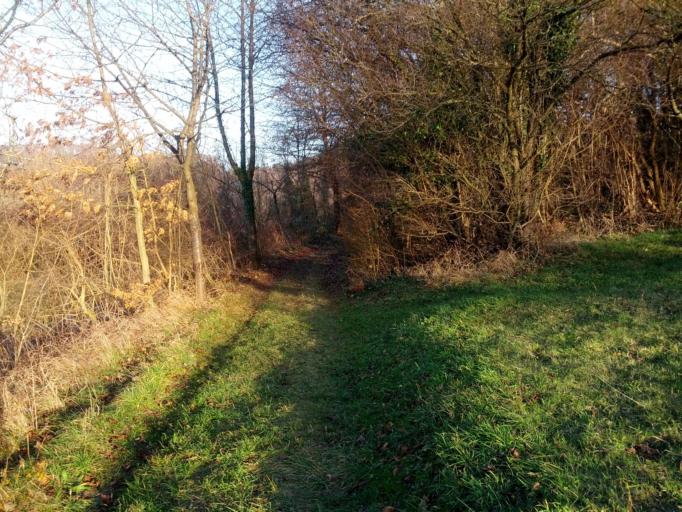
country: DE
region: Baden-Wuerttemberg
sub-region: Freiburg Region
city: Ebringen
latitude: 47.9529
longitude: 7.7831
